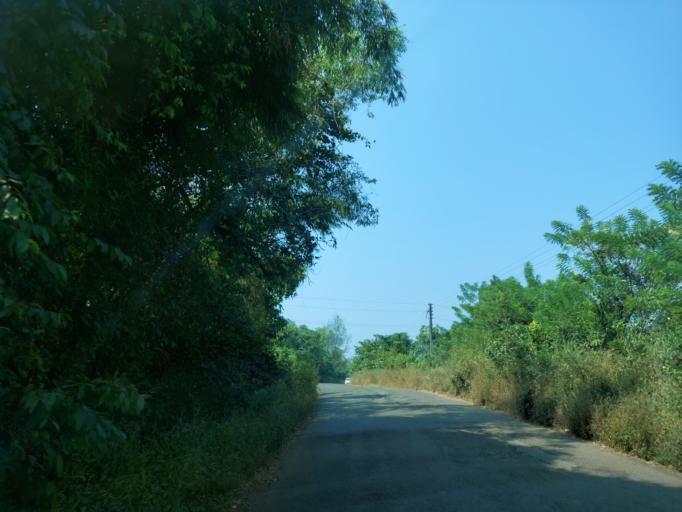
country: IN
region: Maharashtra
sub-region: Sindhudurg
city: Kudal
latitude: 15.9791
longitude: 73.6592
